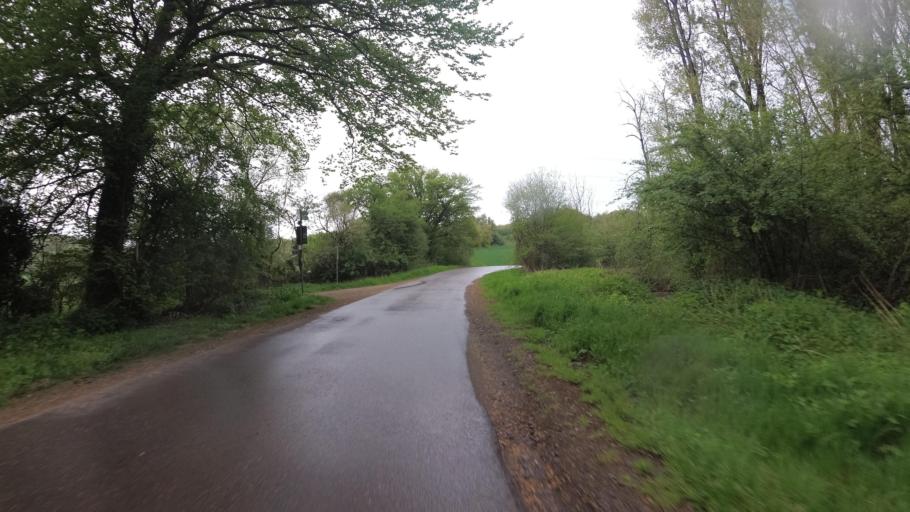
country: FR
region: Lorraine
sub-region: Departement de la Moselle
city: Merten
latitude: 49.2728
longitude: 6.6751
